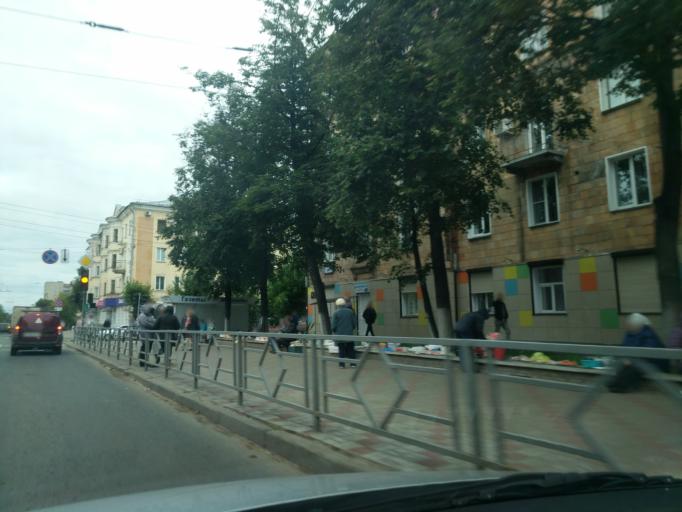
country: RU
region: Kirov
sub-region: Kirovo-Chepetskiy Rayon
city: Kirov
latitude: 58.6079
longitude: 49.6676
